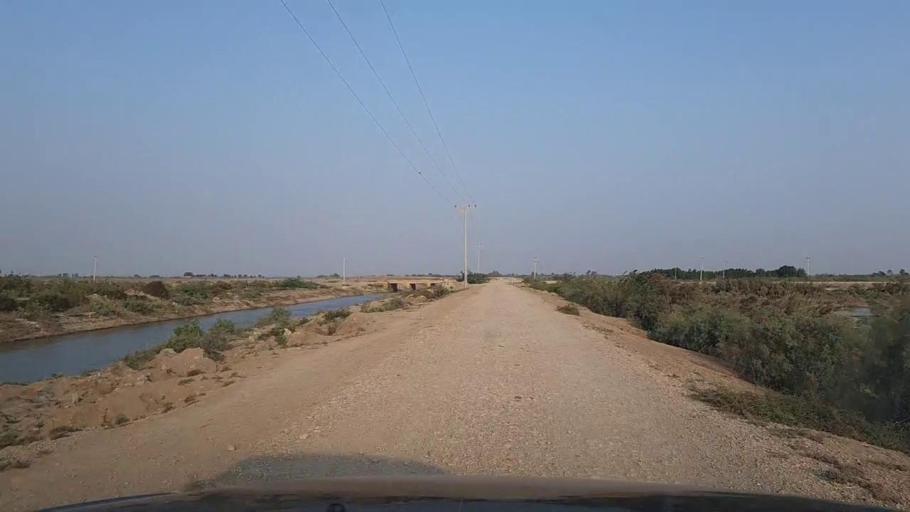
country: PK
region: Sindh
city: Mirpur Sakro
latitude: 24.4179
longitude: 67.7367
